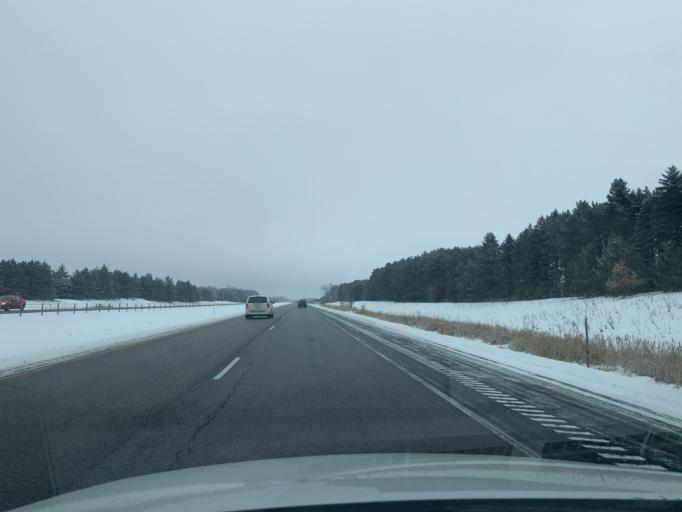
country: US
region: Minnesota
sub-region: Chisago County
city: Branch
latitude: 45.4654
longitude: -92.9960
